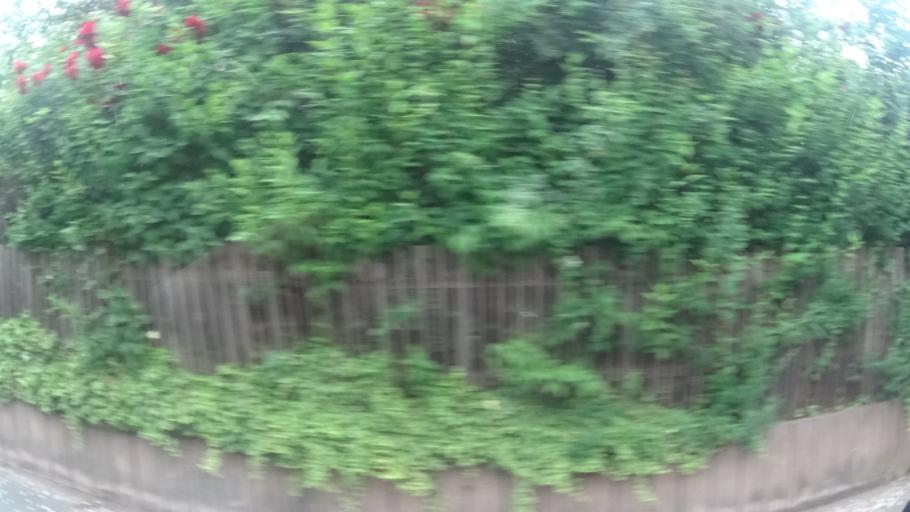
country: DE
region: Bavaria
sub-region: Regierungsbezirk Unterfranken
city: Krombach
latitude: 50.0832
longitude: 9.2066
